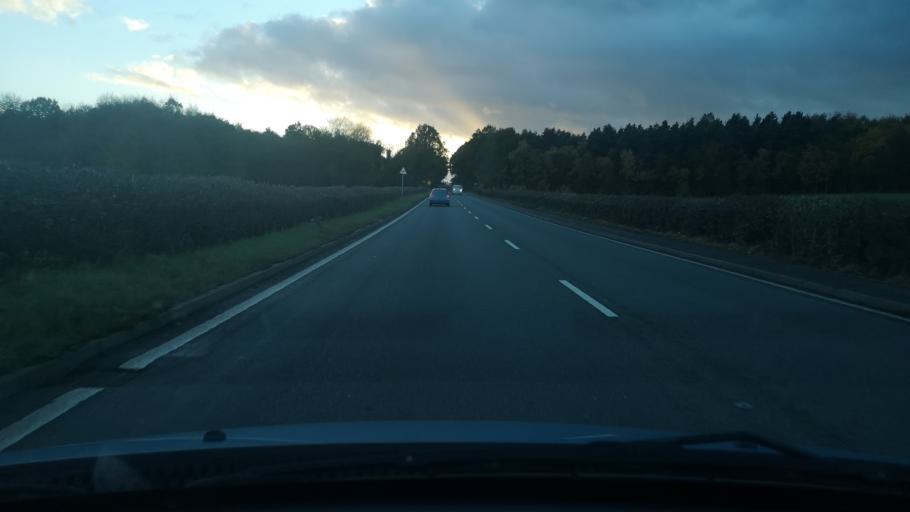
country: GB
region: England
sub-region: City and Borough of Wakefield
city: Crigglestone
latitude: 53.6357
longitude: -1.5533
